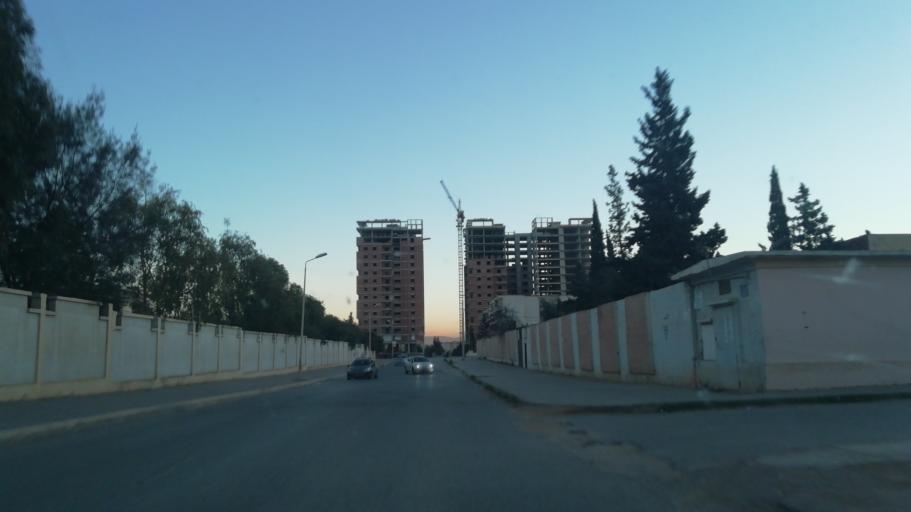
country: DZ
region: Oran
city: Bir el Djir
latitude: 35.6998
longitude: -0.5909
